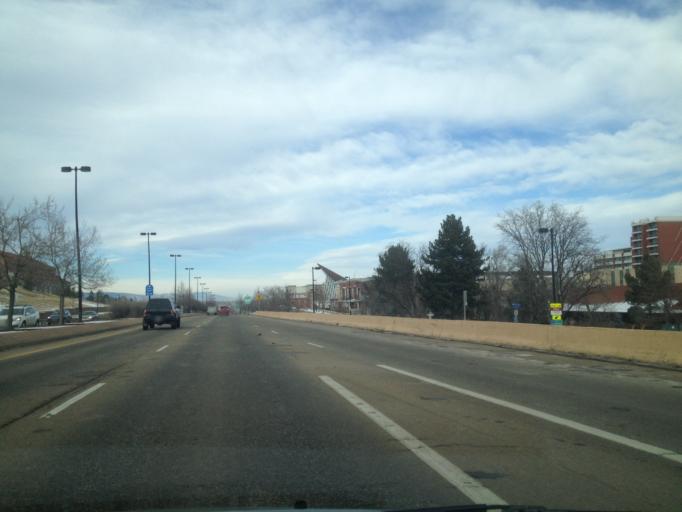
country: US
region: Colorado
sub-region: Boulder County
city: Boulder
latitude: 40.0032
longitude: -105.2585
